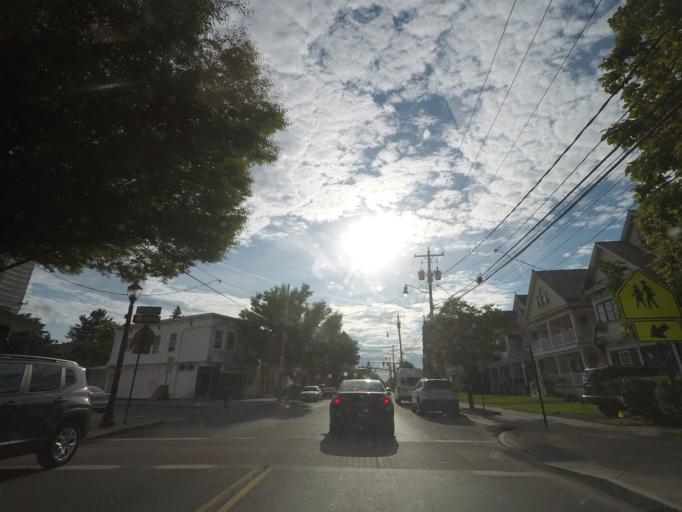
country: US
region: New York
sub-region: Albany County
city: Albany
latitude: 42.6424
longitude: -73.7785
